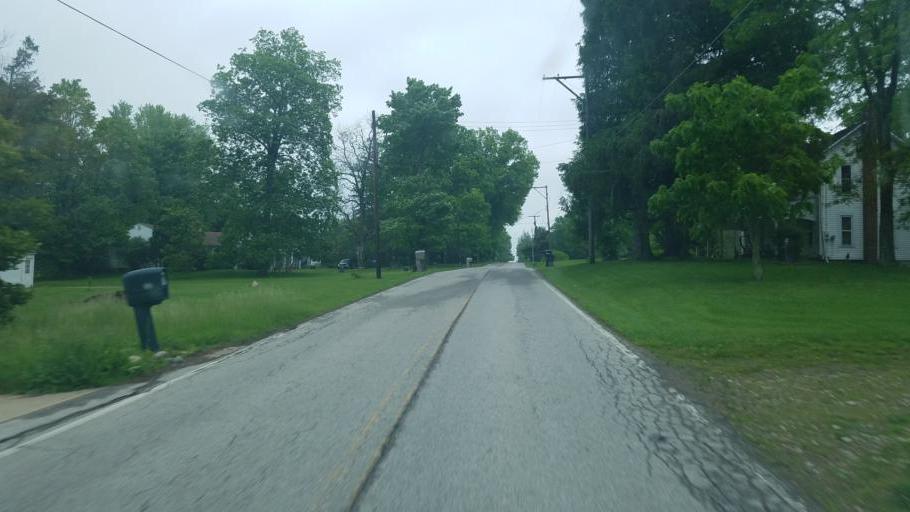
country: US
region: Ohio
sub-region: Richland County
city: Lincoln Heights
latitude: 40.6963
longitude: -82.4686
